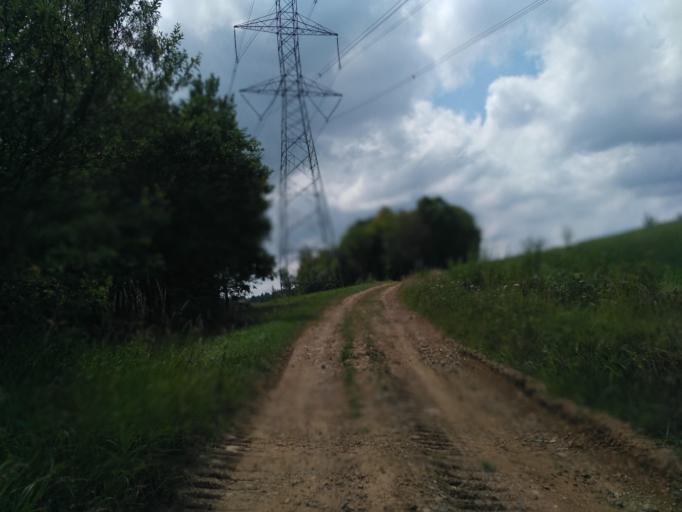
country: PL
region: Subcarpathian Voivodeship
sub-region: Powiat krosnienski
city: Iwonicz-Zdroj
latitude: 49.5864
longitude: 21.7768
